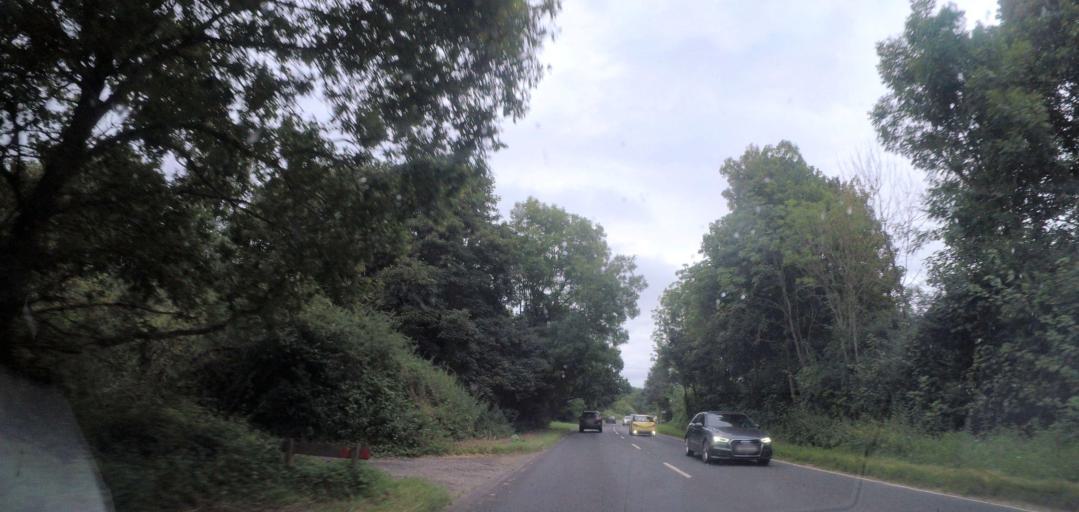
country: GB
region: England
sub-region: Norfolk
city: Spixworth
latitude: 52.6950
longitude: 1.3379
